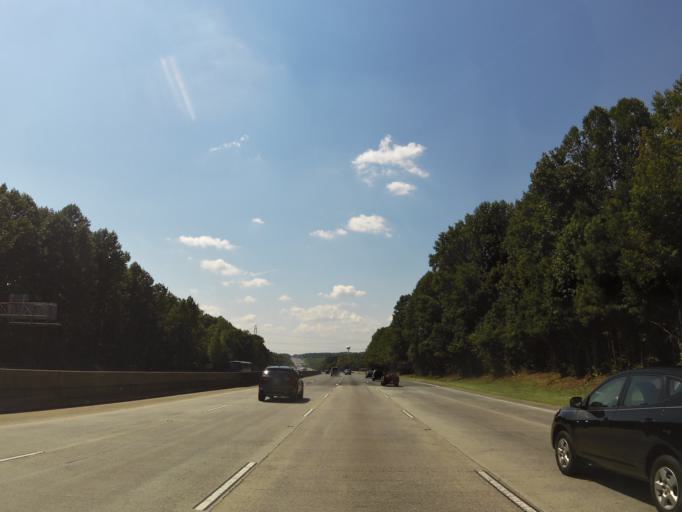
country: US
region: North Carolina
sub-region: Gaston County
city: Belmont
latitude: 35.2581
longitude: -81.0003
